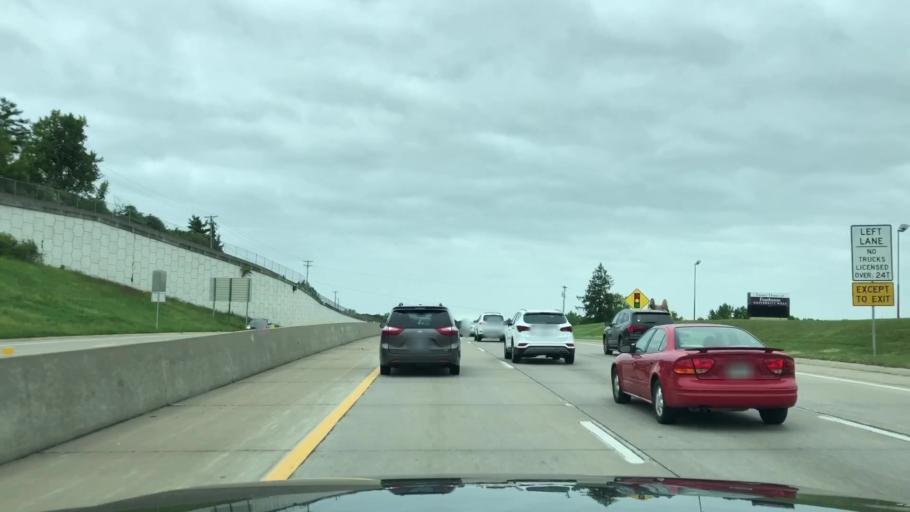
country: US
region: Missouri
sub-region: Saint Louis County
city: Manchester
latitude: 38.6009
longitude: -90.5093
